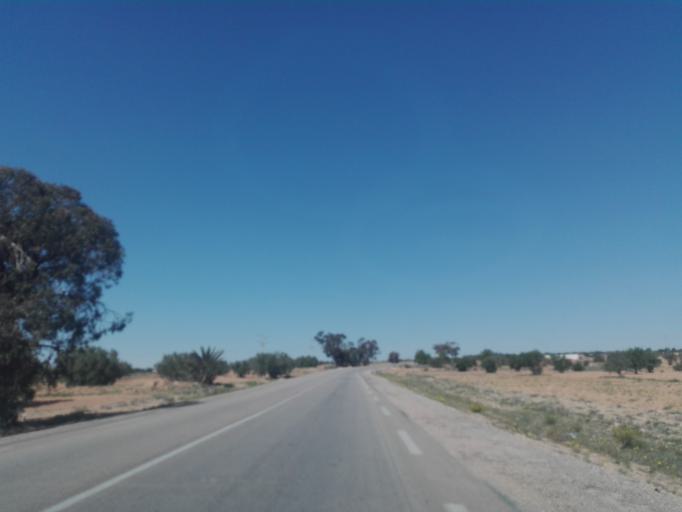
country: TN
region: Safaqis
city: Bi'r `Ali Bin Khalifah
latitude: 34.7466
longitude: 10.3575
